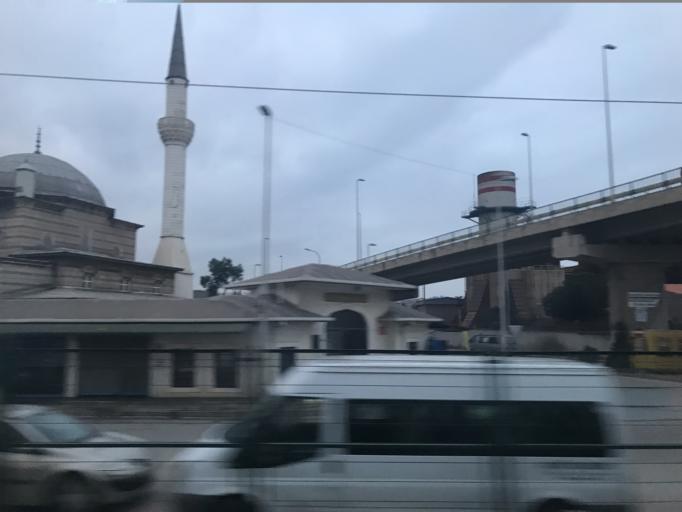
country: TR
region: Kocaeli
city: Darica
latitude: 40.7998
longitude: 29.3791
